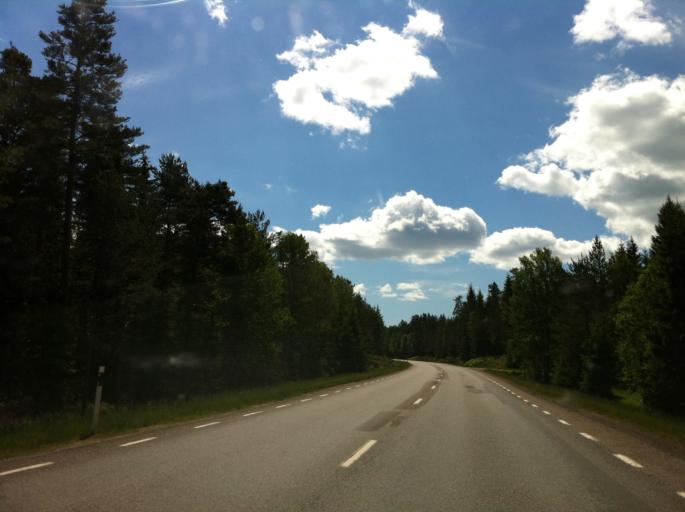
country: SE
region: Vaestra Goetaland
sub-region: Amals Kommun
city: Amal
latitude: 59.0318
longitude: 12.6711
